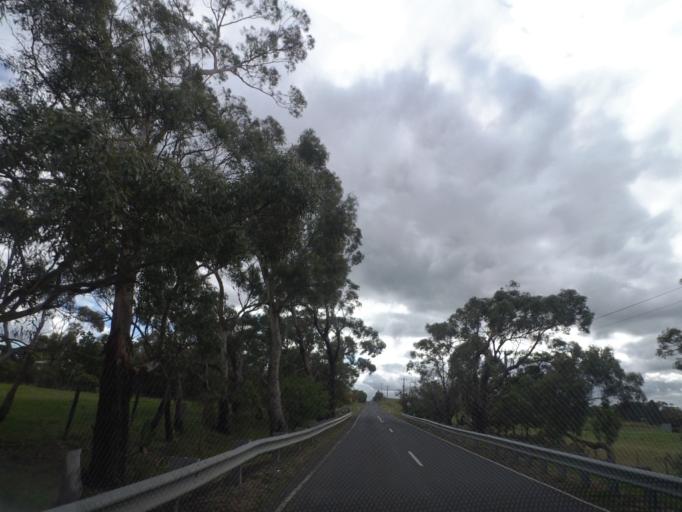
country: AU
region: Victoria
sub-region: Whittlesea
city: Whittlesea
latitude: -37.5217
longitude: 145.0489
